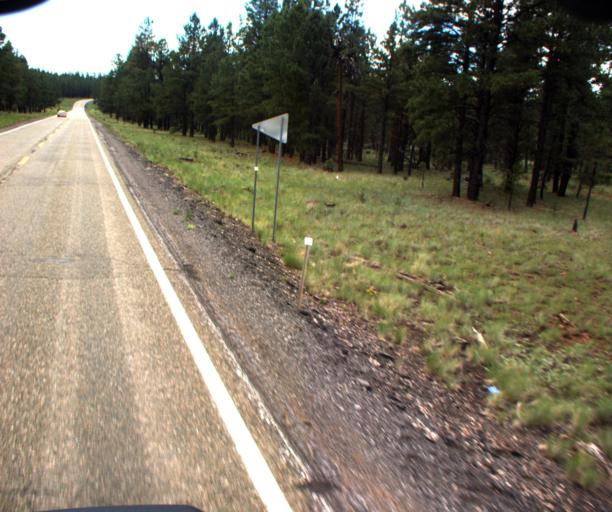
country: US
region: Arizona
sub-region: Coconino County
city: Parks
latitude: 35.3618
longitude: -111.7912
